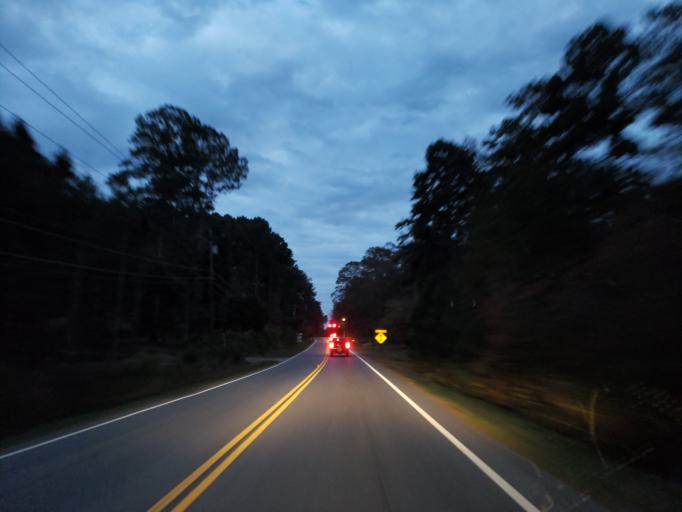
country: US
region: Georgia
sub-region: Cobb County
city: Powder Springs
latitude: 33.9167
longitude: -84.6909
